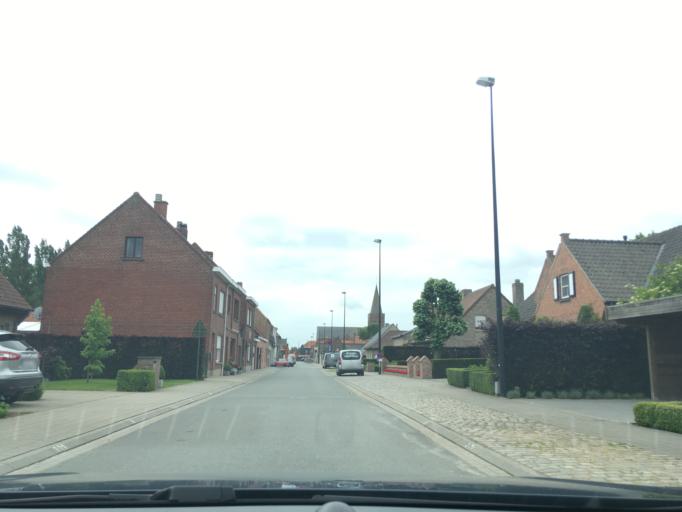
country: BE
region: Flanders
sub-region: Provincie West-Vlaanderen
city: Moorslede
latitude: 50.8696
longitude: 3.0883
